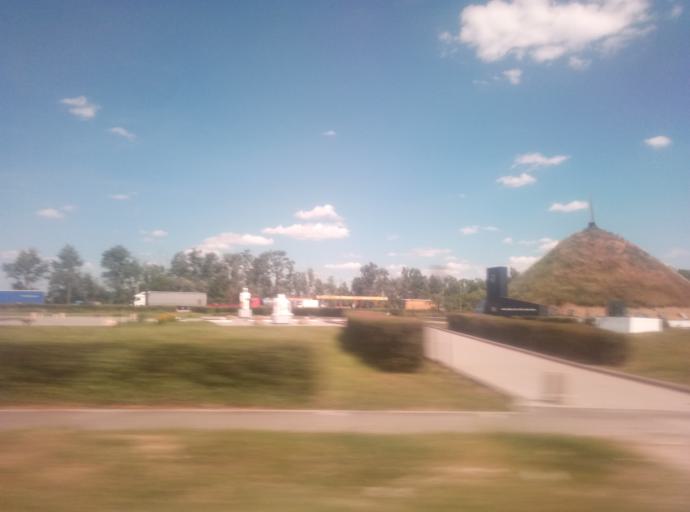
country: RU
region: Tula
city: Kireyevsk
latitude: 54.0194
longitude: 37.9080
